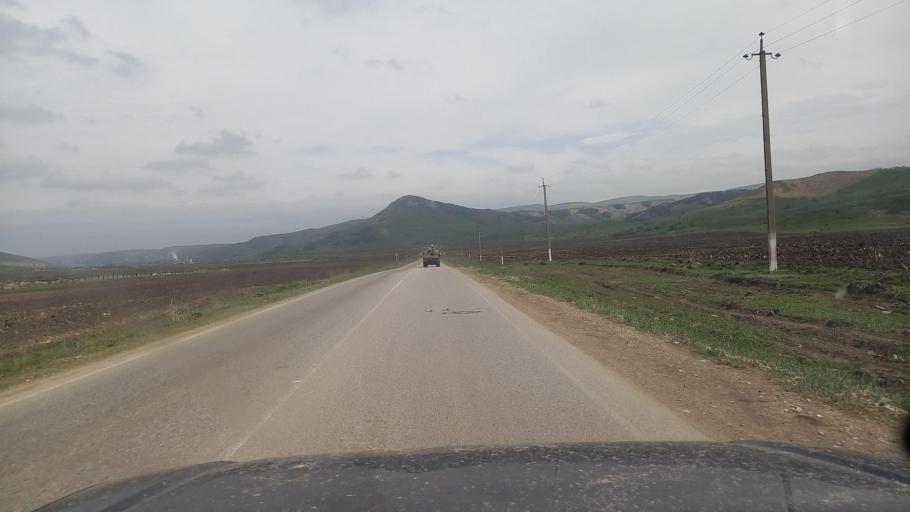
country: RU
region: Kabardino-Balkariya
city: Kamennomostskoye
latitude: 43.7288
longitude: 43.1050
